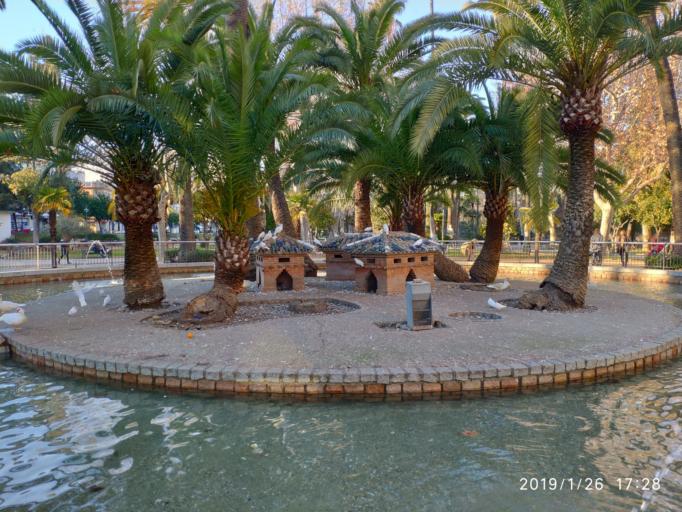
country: ES
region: Andalusia
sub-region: Province of Cordoba
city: Cordoba
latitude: 37.8870
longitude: -4.7853
